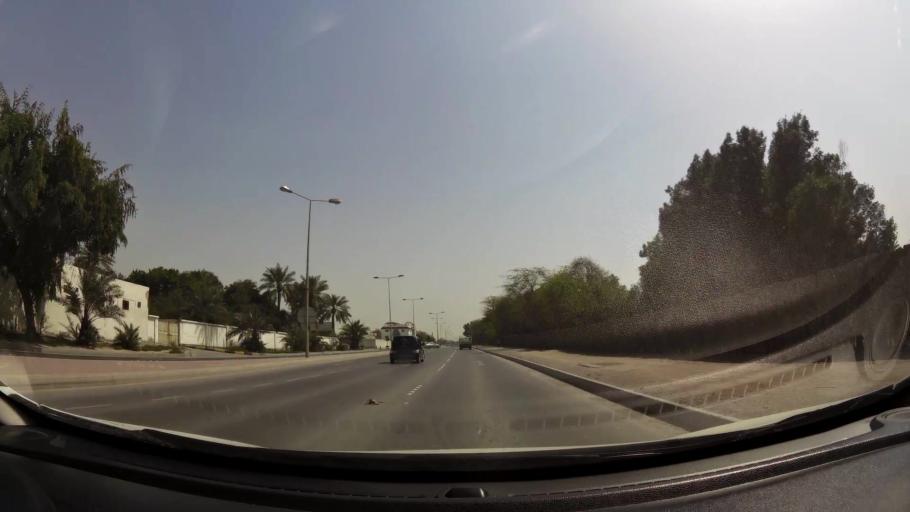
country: BH
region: Manama
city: Jidd Hafs
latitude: 26.2020
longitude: 50.4593
